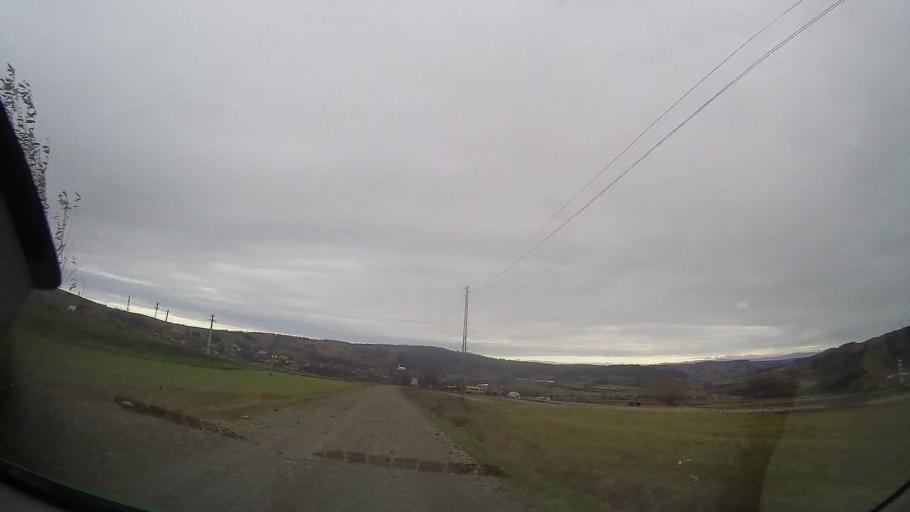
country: RO
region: Mures
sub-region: Comuna Bala
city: Bala
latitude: 46.7008
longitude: 24.4936
